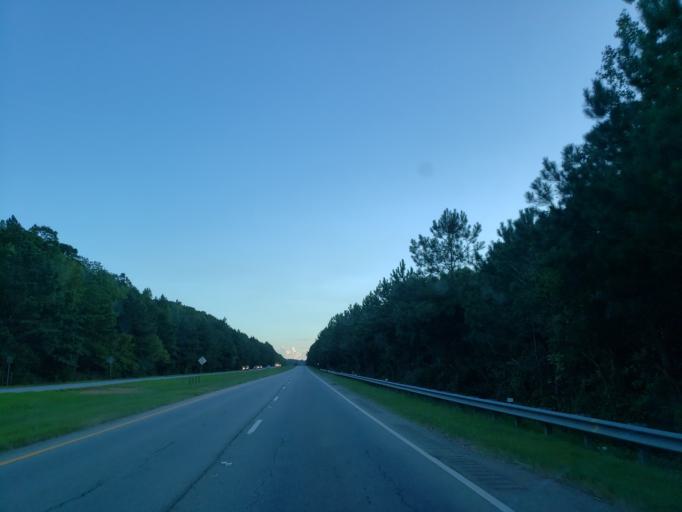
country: US
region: Georgia
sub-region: Floyd County
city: Rome
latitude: 34.2307
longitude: -85.1172
